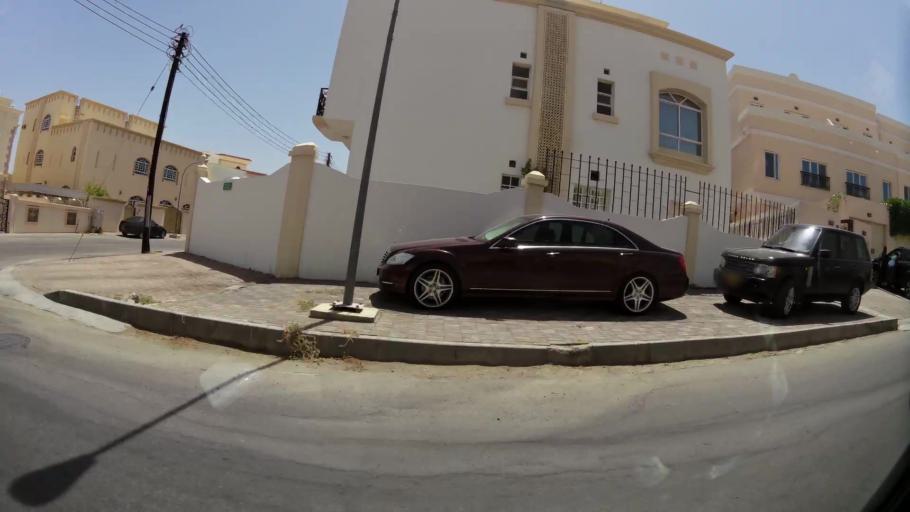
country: OM
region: Muhafazat Masqat
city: Bawshar
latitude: 23.5879
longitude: 58.4484
